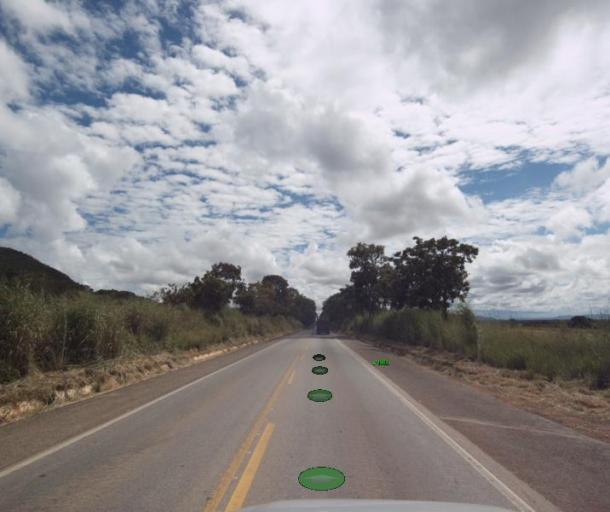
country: BR
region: Goias
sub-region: Uruacu
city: Uruacu
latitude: -14.3952
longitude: -49.1577
